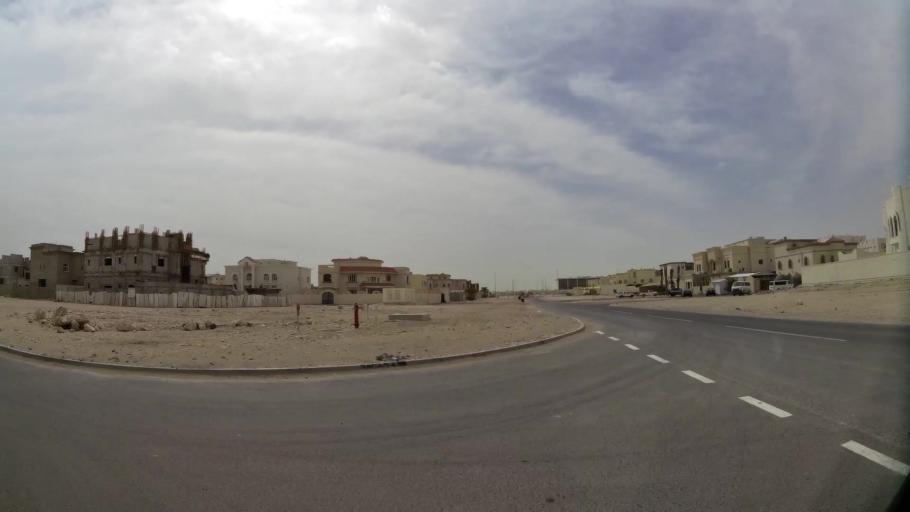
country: QA
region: Al Wakrah
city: Al Wukayr
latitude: 25.2008
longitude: 51.4605
